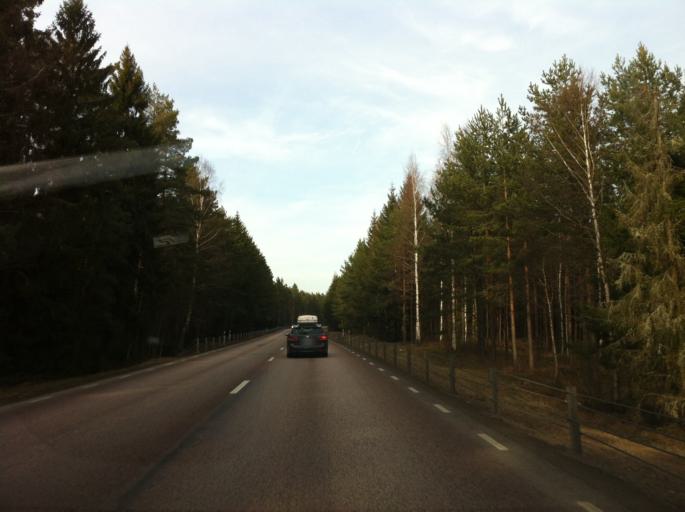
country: SE
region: Vaestra Goetaland
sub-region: Gullspangs Kommun
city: Gullspang
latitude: 59.0769
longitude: 14.1568
